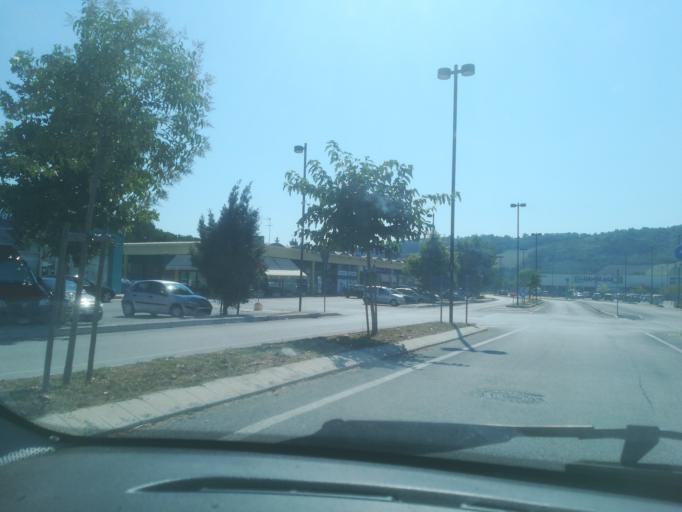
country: IT
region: The Marches
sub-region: Provincia di Macerata
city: Villa Potenza
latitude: 43.3389
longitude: 13.4371
